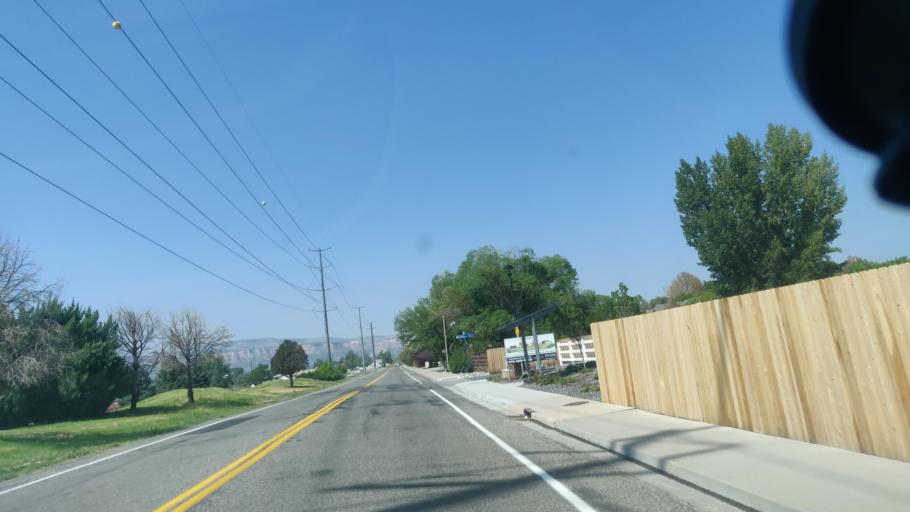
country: US
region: Colorado
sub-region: Mesa County
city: Grand Junction
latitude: 39.0991
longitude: -108.5842
